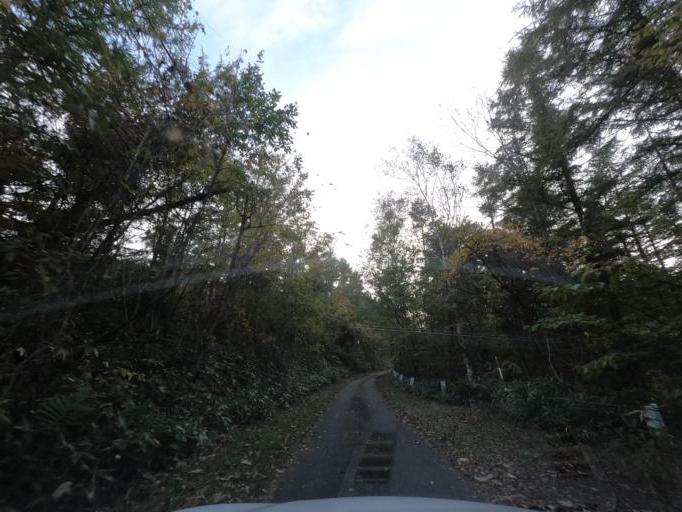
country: JP
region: Hokkaido
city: Obihiro
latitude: 42.5864
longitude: 143.3141
